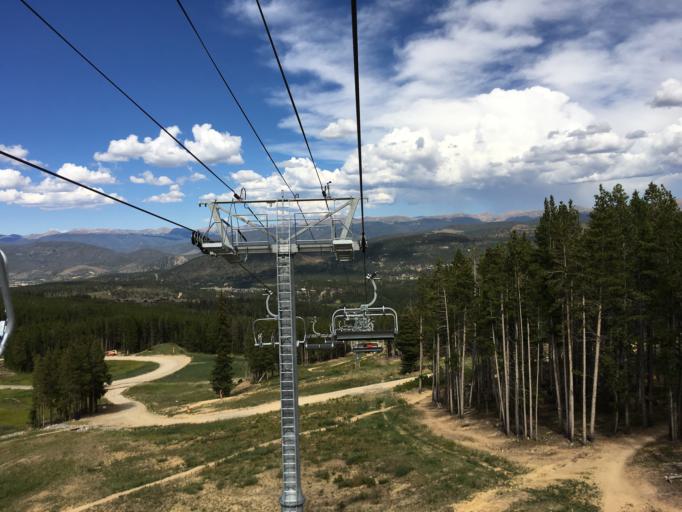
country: US
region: Colorado
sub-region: Summit County
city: Breckenridge
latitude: 39.4761
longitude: -106.0761
